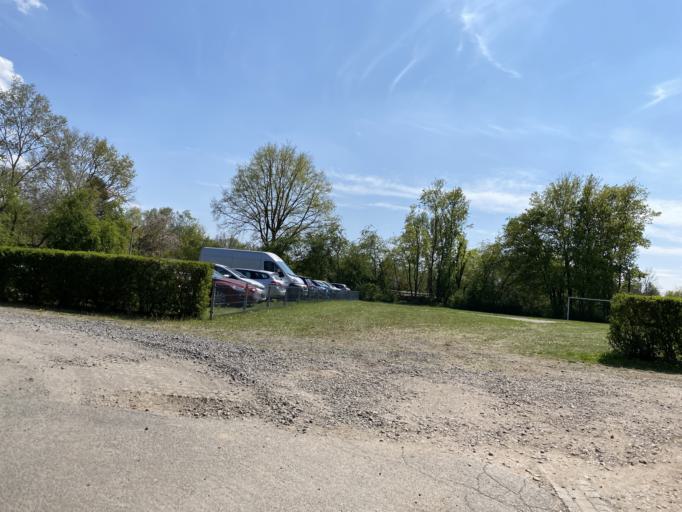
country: DE
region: Hesse
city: Langen
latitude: 49.9975
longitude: 8.6852
